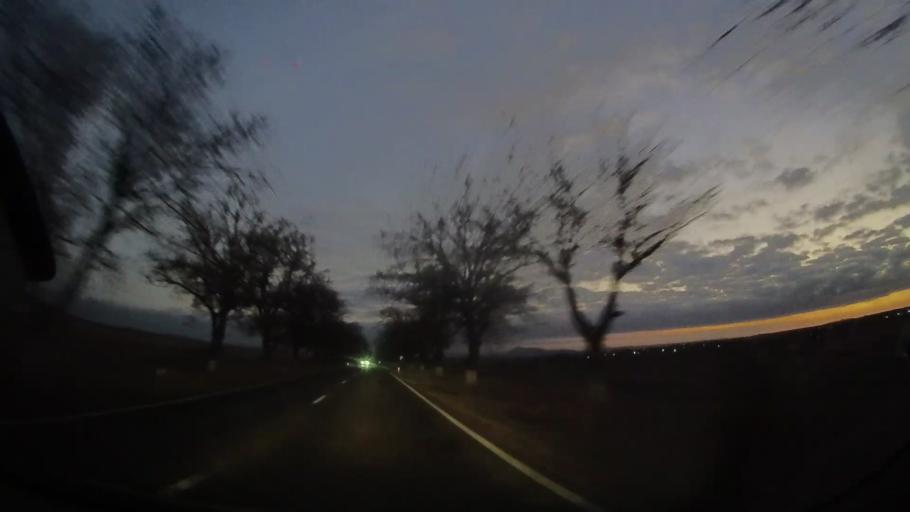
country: RO
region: Tulcea
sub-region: Comuna Frecatei
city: Cataloi
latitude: 45.0980
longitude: 28.7419
